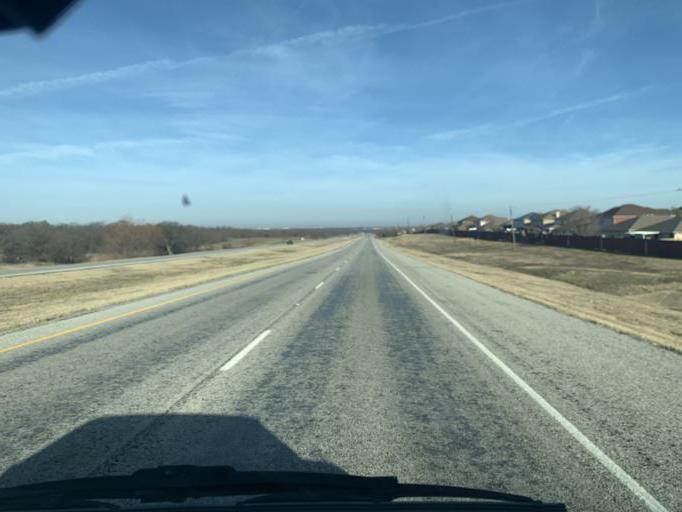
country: US
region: Texas
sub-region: Dallas County
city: Cedar Hill
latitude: 32.6449
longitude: -96.9742
